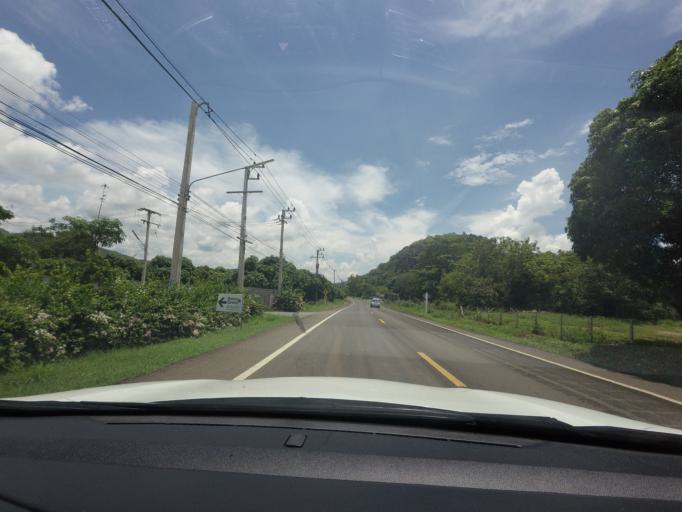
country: TH
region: Sara Buri
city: Muak Lek
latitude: 14.5860
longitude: 101.2481
